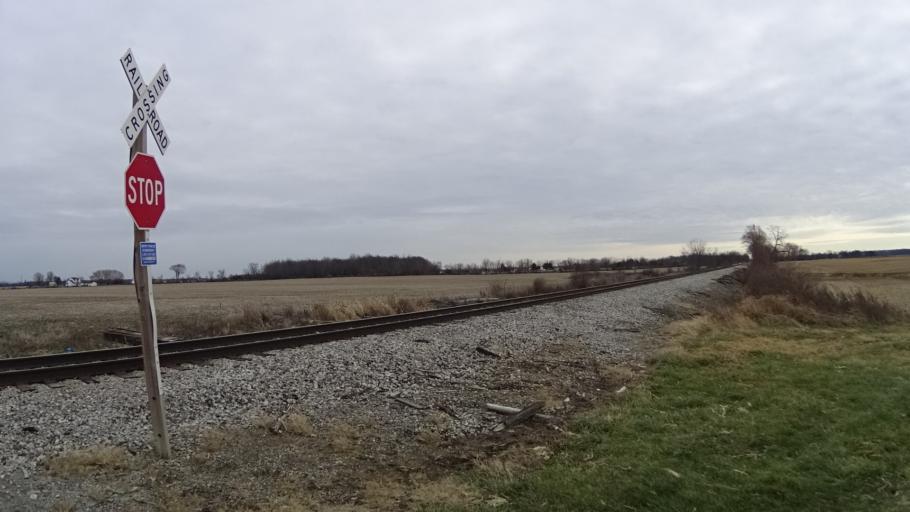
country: US
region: Ohio
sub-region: Lorain County
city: Wellington
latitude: 41.1430
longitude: -82.1940
